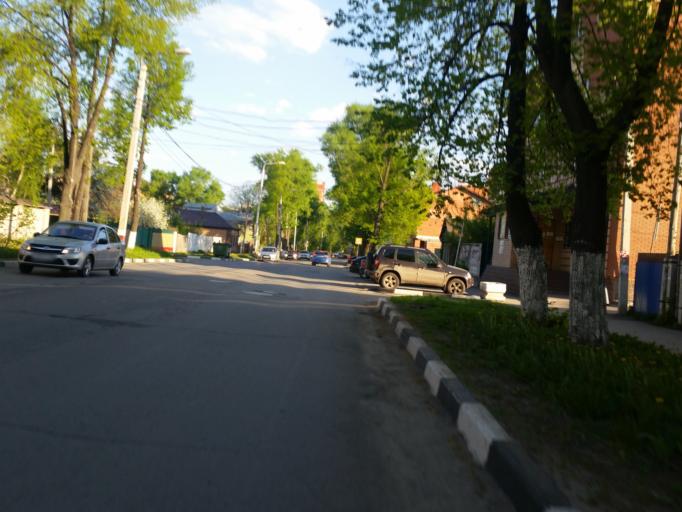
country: RU
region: Ulyanovsk
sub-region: Ulyanovskiy Rayon
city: Ulyanovsk
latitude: 54.3262
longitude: 48.3993
